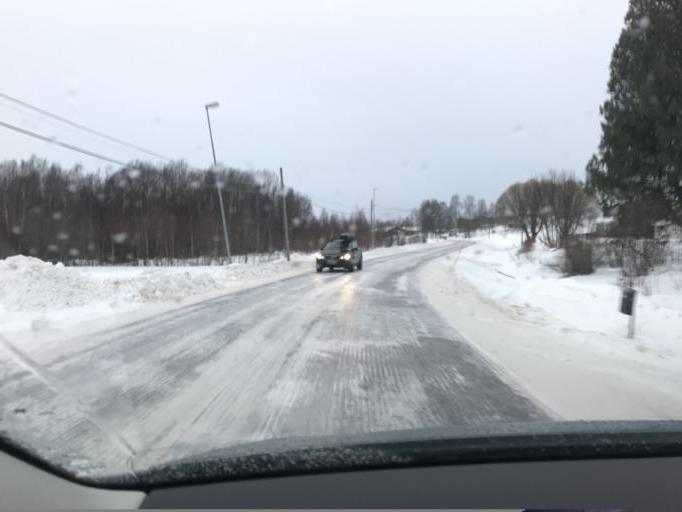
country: SE
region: Norrbotten
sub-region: Lulea Kommun
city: Sodra Sunderbyn
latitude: 65.6610
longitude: 21.9313
